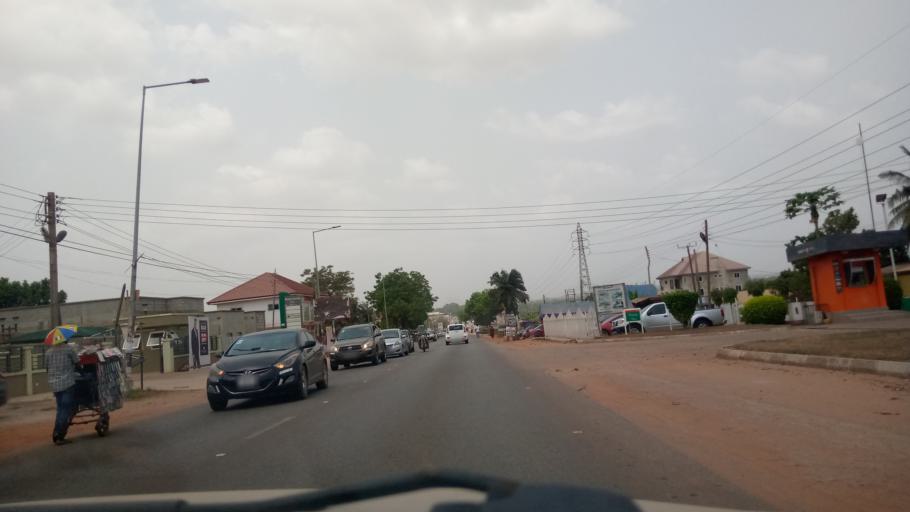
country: GH
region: Greater Accra
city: Dome
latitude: 5.6675
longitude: -0.2081
